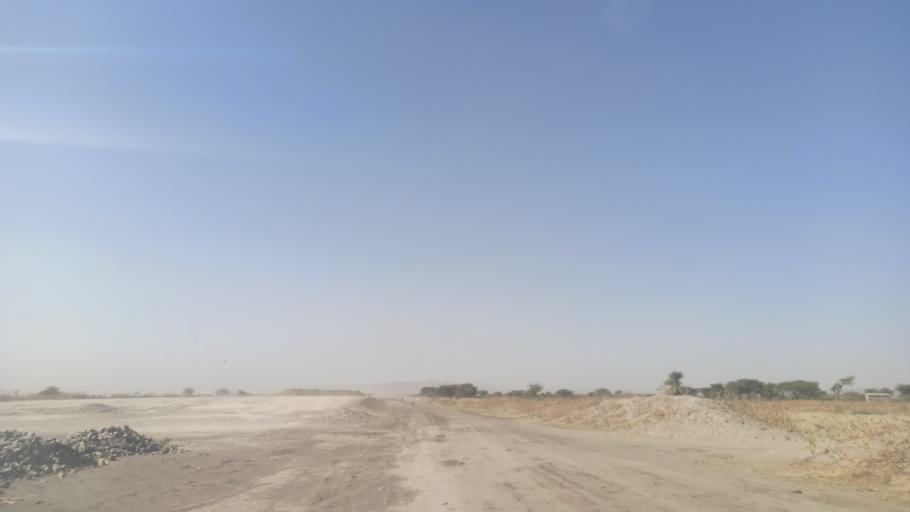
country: ET
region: Oromiya
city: Ziway
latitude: 7.7350
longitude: 38.6235
